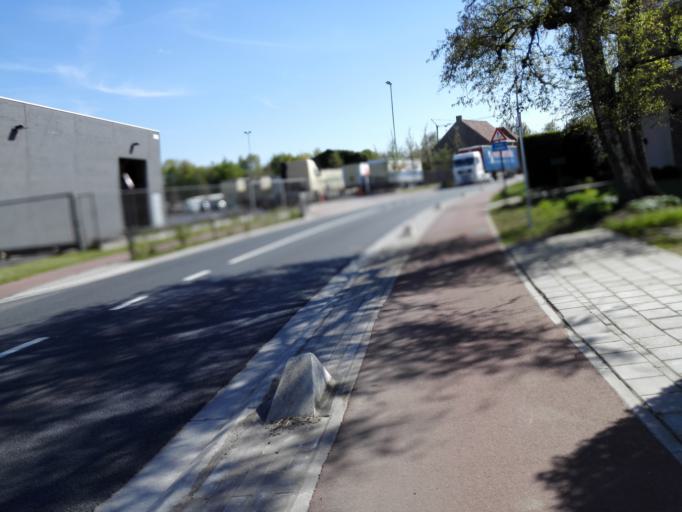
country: BE
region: Flanders
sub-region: Provincie West-Vlaanderen
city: Oostrozebeke
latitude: 50.9157
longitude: 3.3553
